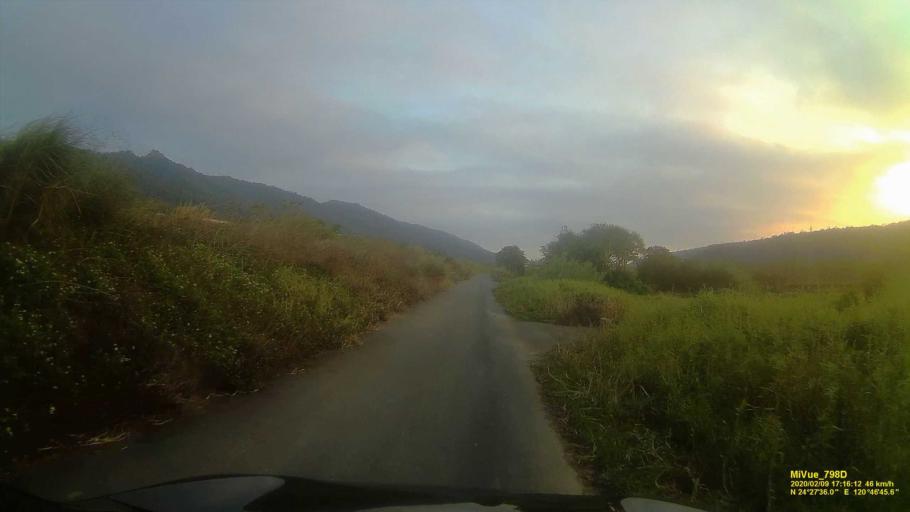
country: TW
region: Taiwan
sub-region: Miaoli
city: Miaoli
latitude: 24.4598
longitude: 120.7794
